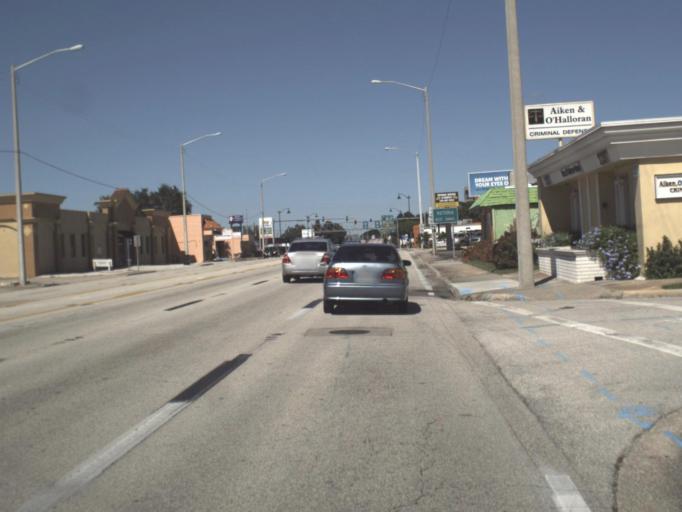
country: US
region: Florida
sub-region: Lee County
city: North Fort Myers
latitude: 26.6351
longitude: -81.8725
